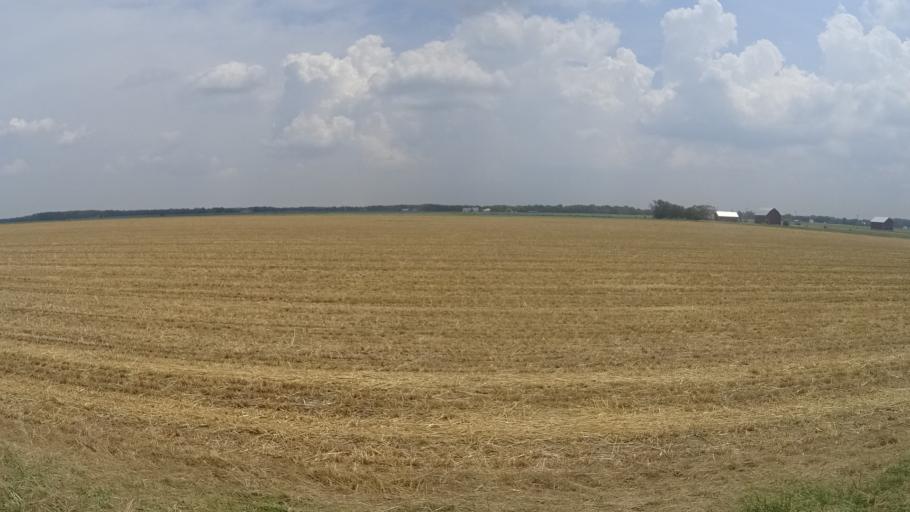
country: US
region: Ohio
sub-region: Huron County
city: Monroeville
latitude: 41.2889
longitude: -82.6921
